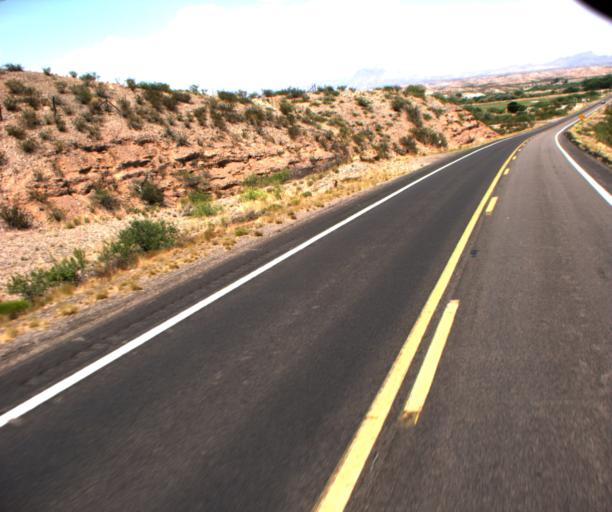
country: US
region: Arizona
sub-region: Greenlee County
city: Clifton
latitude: 32.7397
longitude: -109.1398
